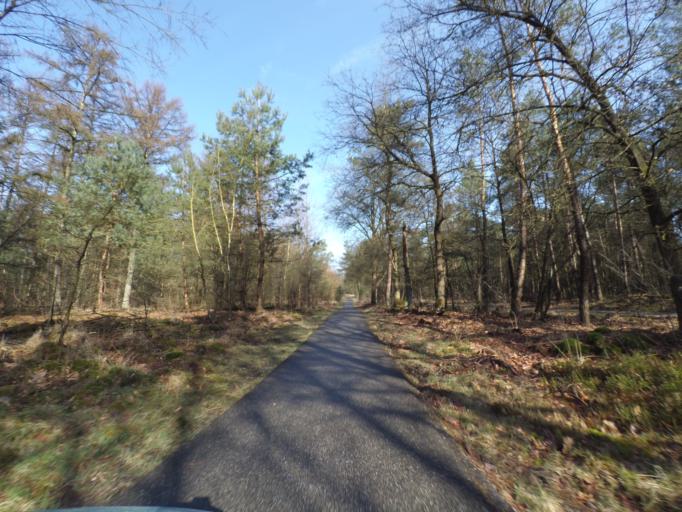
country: NL
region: Gelderland
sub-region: Gemeente Apeldoorn
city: Uddel
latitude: 52.2014
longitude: 5.8120
